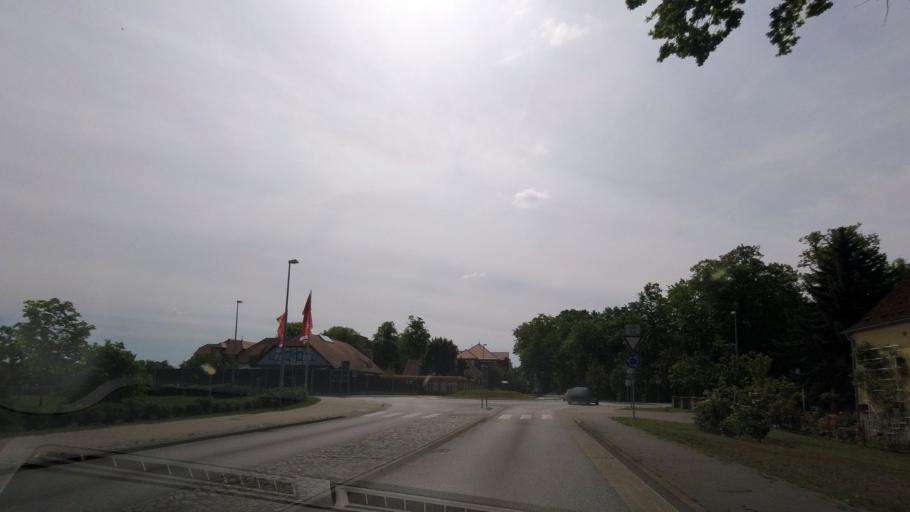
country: DE
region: Brandenburg
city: Wittstock
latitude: 53.1534
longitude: 12.4850
